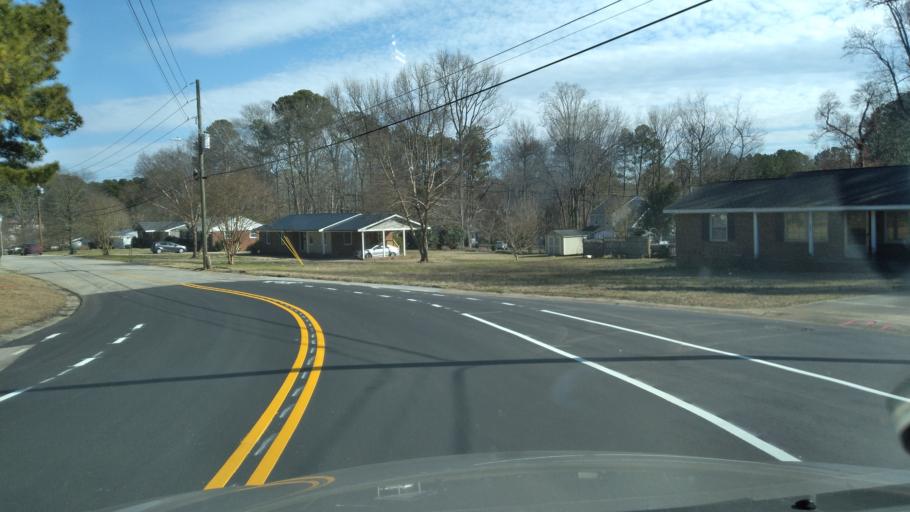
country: US
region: North Carolina
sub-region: Wake County
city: Garner
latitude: 35.6977
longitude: -78.6203
